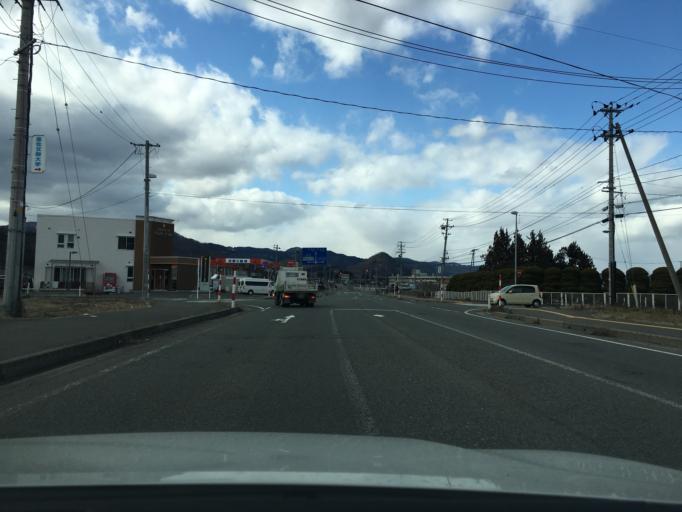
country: JP
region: Yamagata
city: Kaminoyama
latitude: 38.2088
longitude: 140.3018
